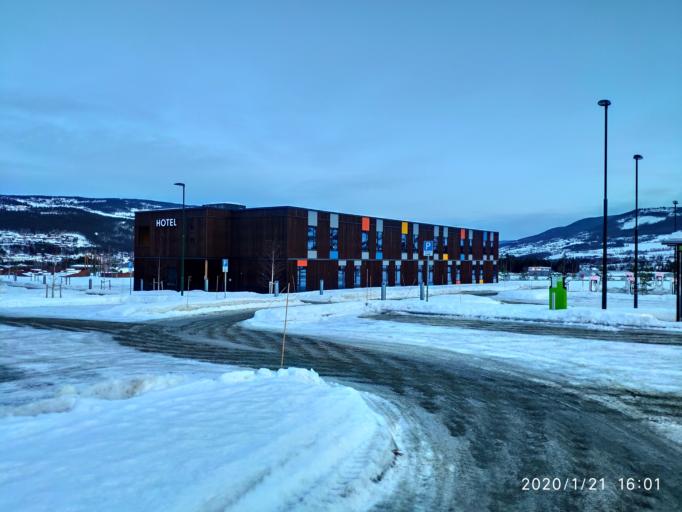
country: NO
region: Oppland
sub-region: Nord-Fron
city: Vinstra
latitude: 61.5908
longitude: 9.7207
